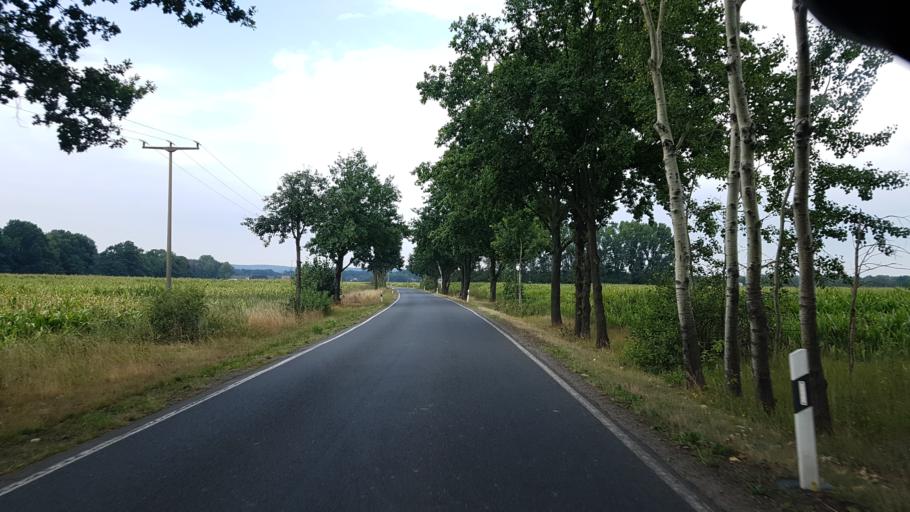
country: DE
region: Brandenburg
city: Lindenau
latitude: 51.4129
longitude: 13.7236
